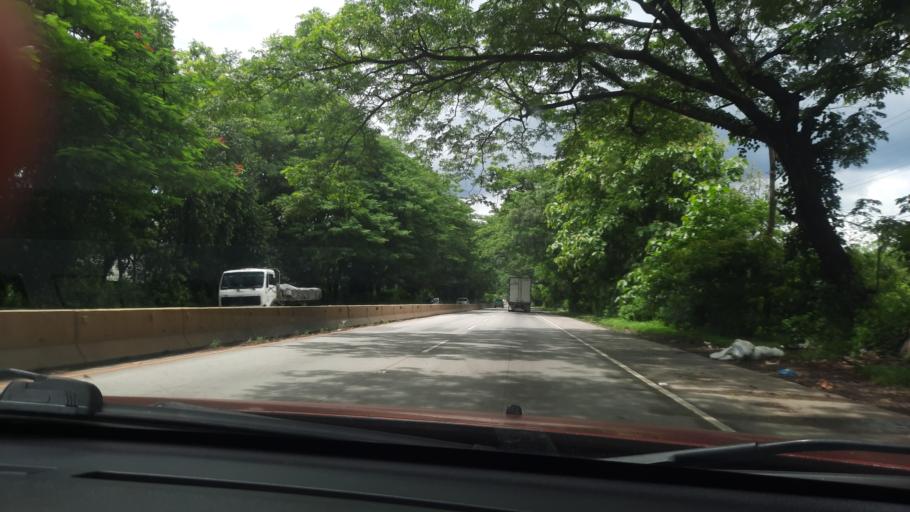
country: SV
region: Sonsonate
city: Sonzacate
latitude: 13.7242
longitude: -89.7045
